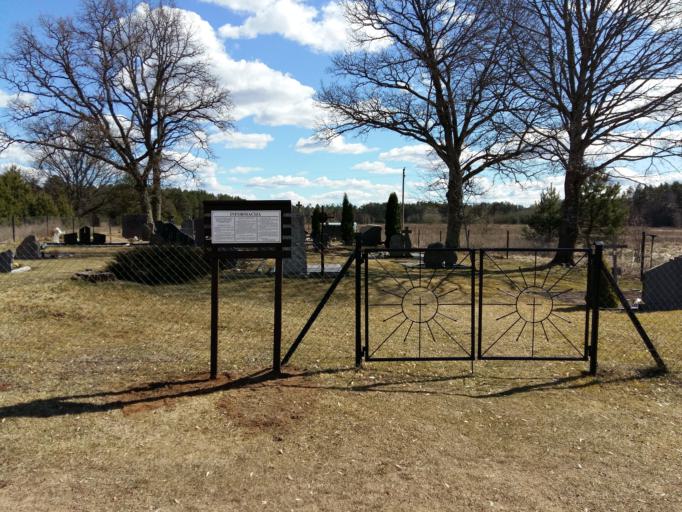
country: LT
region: Alytaus apskritis
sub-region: Alytaus rajonas
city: Daugai
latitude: 54.1519
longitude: 24.2440
